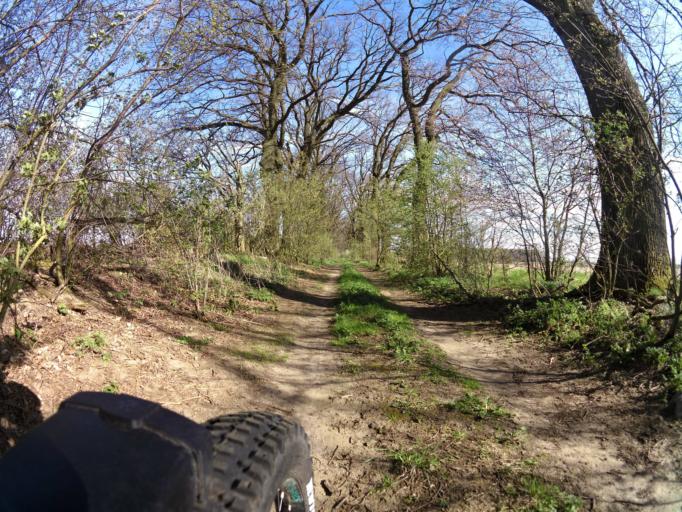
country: PL
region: West Pomeranian Voivodeship
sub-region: Powiat lobeski
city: Resko
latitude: 53.7809
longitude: 15.5524
